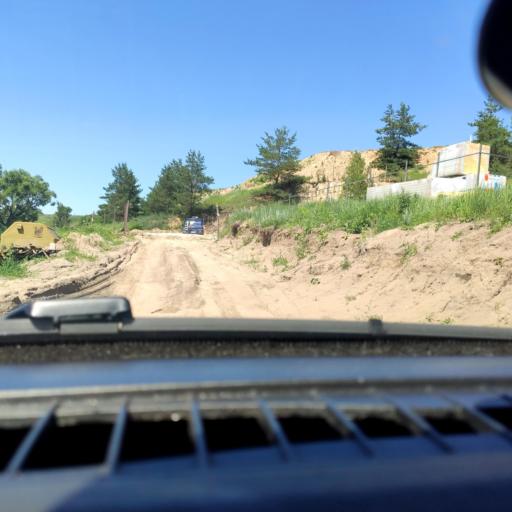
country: RU
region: Voronezj
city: Podgornoye
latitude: 51.7977
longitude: 39.1359
